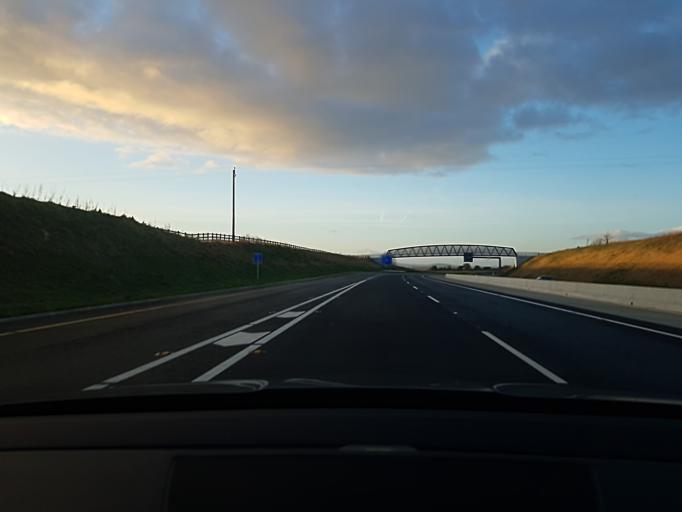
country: IE
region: Connaught
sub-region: County Galway
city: Tuam
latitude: 53.4048
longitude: -8.8213
